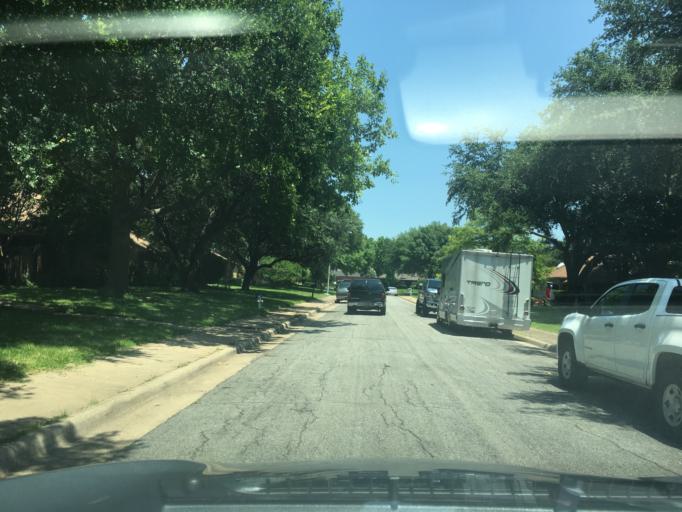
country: US
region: Texas
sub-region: Dallas County
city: Richardson
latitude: 32.9205
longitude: -96.7105
